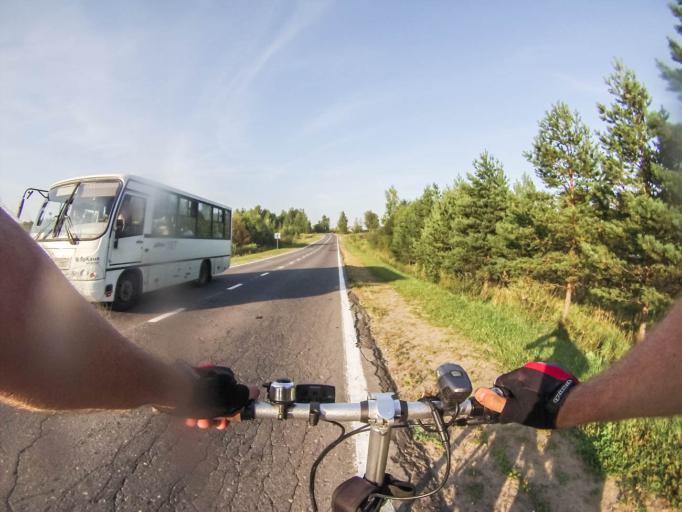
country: RU
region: Jaroslavl
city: Myshkin
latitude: 57.7469
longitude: 38.4326
